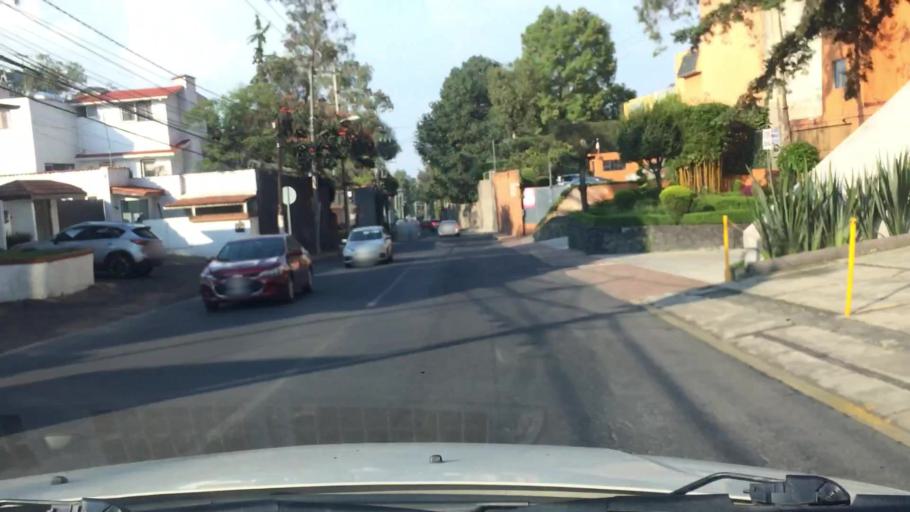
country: MX
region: Mexico City
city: Magdalena Contreras
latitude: 19.3244
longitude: -99.2181
